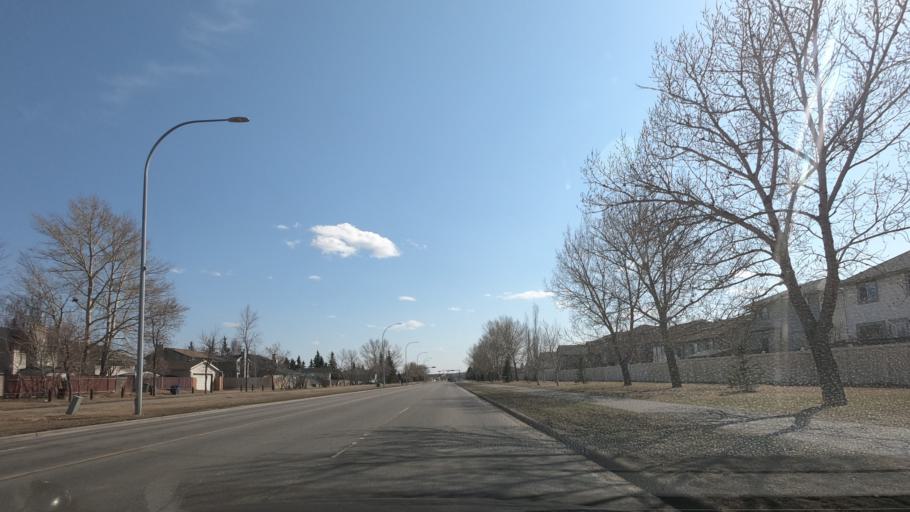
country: CA
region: Alberta
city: Airdrie
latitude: 51.2752
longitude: -113.9899
